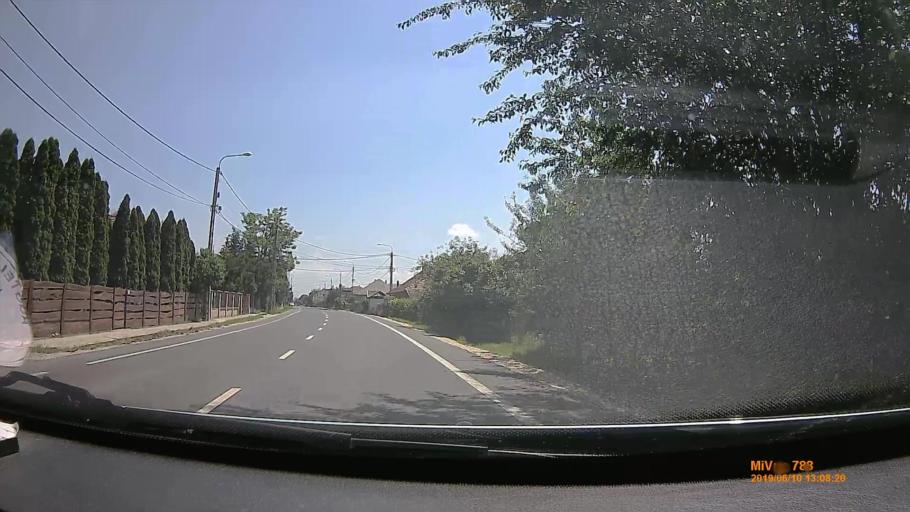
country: HU
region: Borsod-Abauj-Zemplen
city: Hernadnemeti
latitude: 48.0806
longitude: 20.9714
